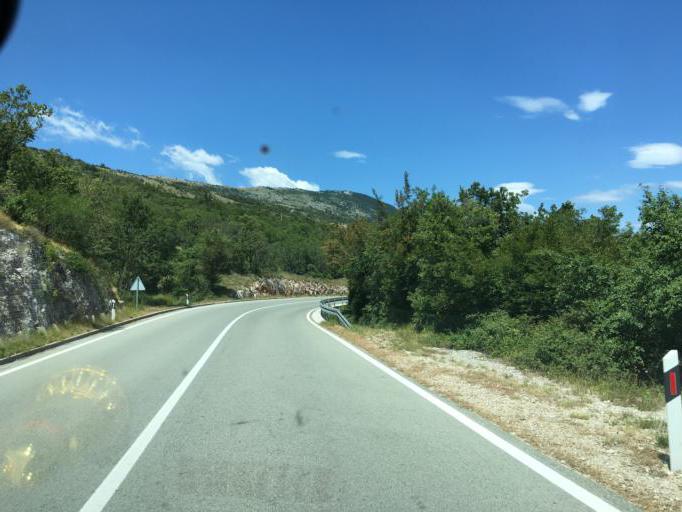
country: HR
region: Istarska
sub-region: Grad Labin
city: Rabac
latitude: 45.1431
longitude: 14.2130
